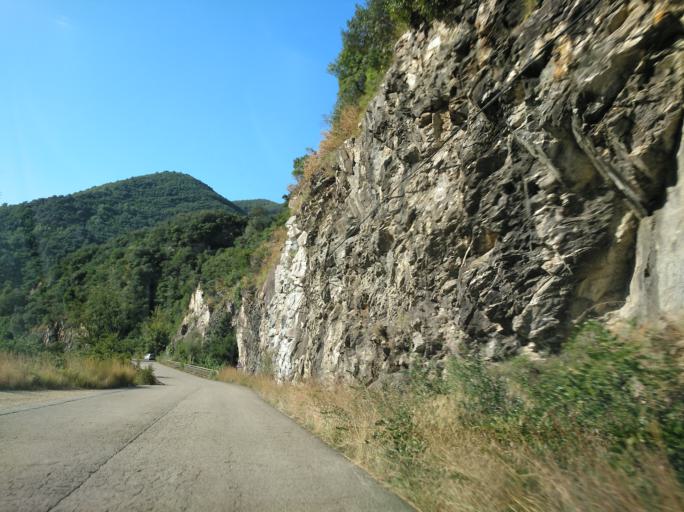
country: ES
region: Catalonia
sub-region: Provincia de Girona
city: la Cellera de Ter
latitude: 41.9803
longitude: 2.5984
